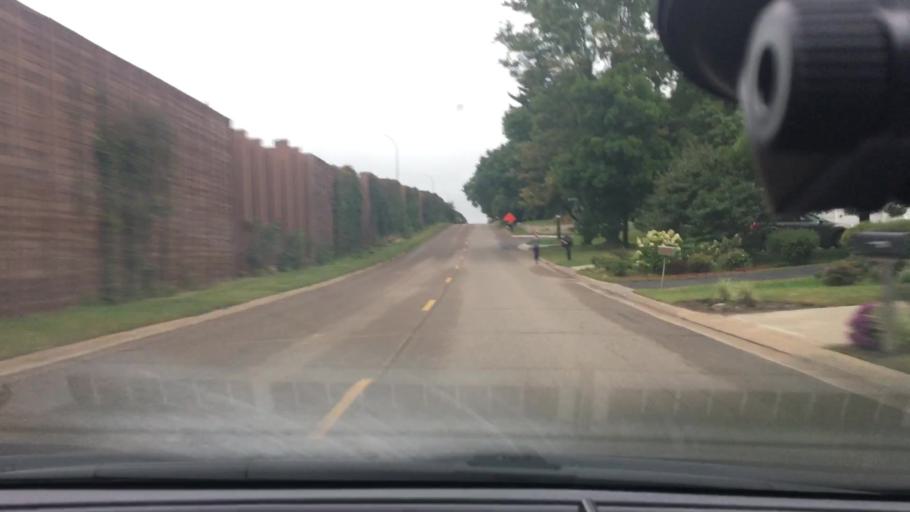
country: US
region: Minnesota
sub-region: Hennepin County
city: New Hope
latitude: 44.9974
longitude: -93.4005
